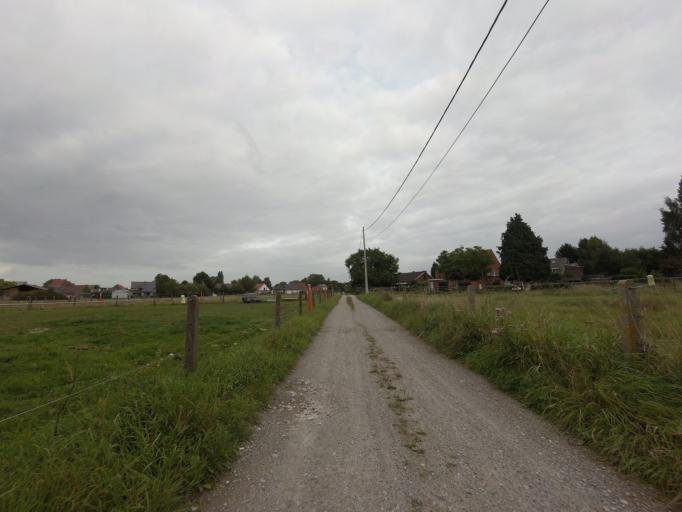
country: BE
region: Flanders
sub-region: Provincie Vlaams-Brabant
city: Londerzeel
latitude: 50.9782
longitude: 4.3282
